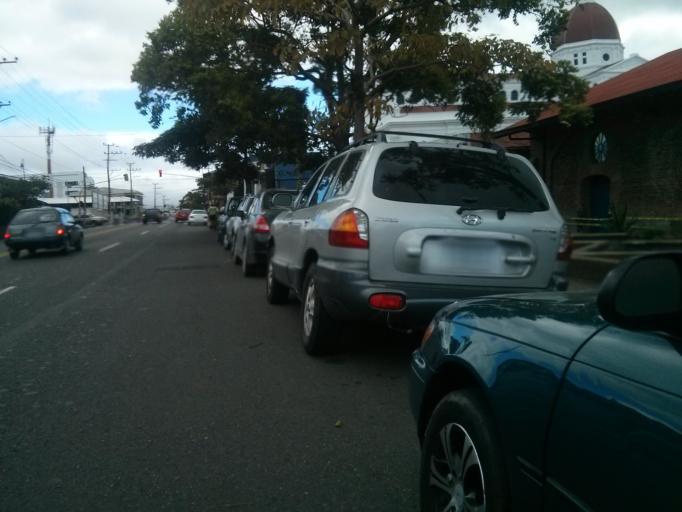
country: CR
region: San Jose
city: Calle Blancos
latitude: 9.9360
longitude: -84.0671
